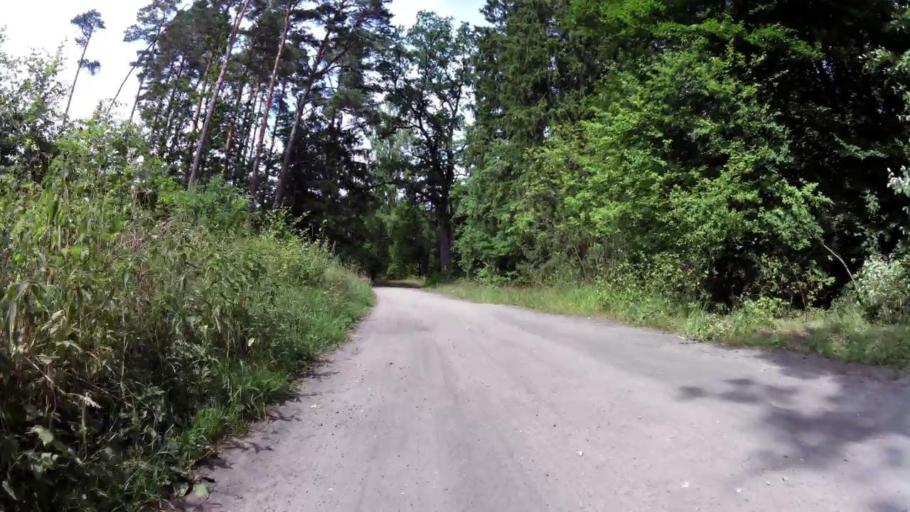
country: PL
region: West Pomeranian Voivodeship
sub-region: Powiat lobeski
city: Lobez
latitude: 53.5967
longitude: 15.6566
